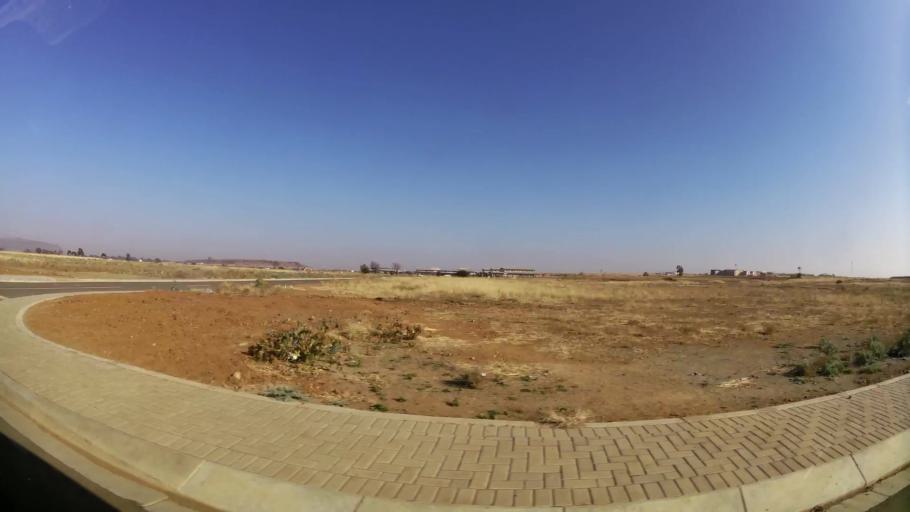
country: ZA
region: Orange Free State
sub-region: Mangaung Metropolitan Municipality
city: Bloemfontein
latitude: -29.1899
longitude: 26.2190
